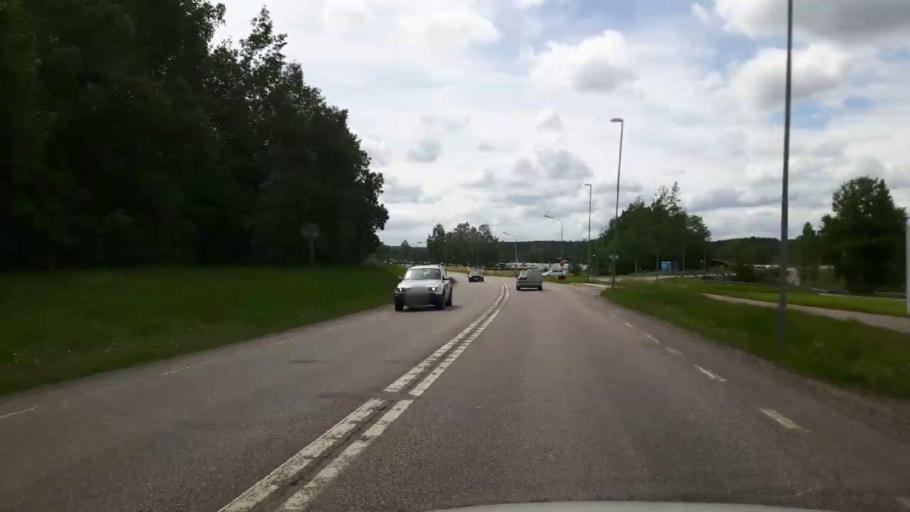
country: SE
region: Vaestmanland
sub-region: Fagersta Kommun
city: Fagersta
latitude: 59.9821
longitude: 15.8001
